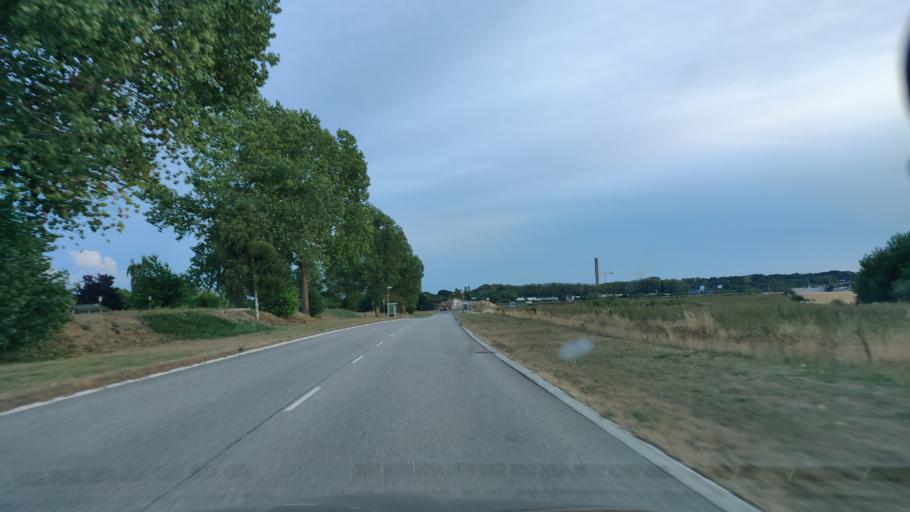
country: DK
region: Capital Region
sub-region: Hoje-Taastrup Kommune
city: Flong
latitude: 55.6603
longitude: 12.1755
